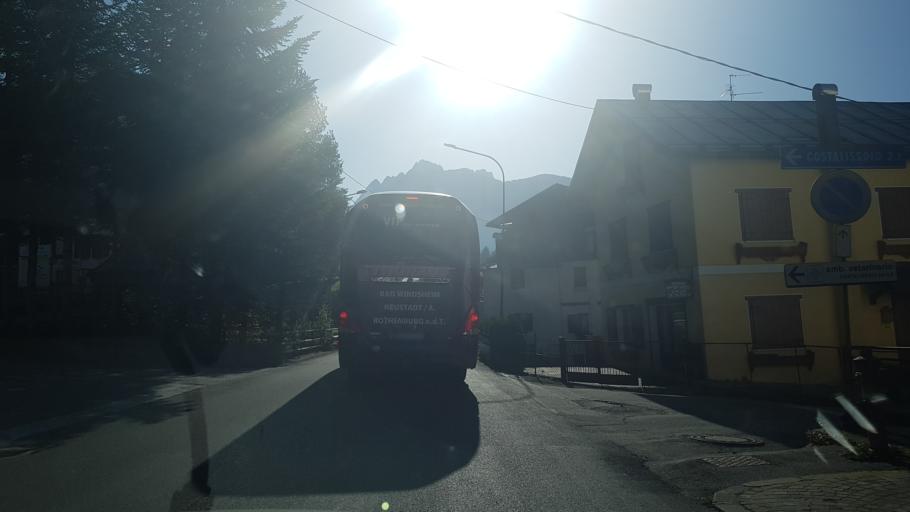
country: IT
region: Veneto
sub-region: Provincia di Belluno
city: San Nicolo Comelico
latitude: 46.5763
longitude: 12.5324
